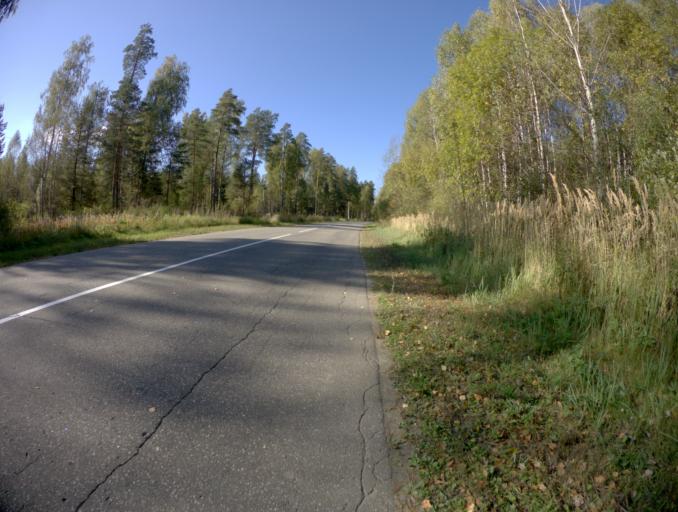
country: RU
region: Vladimir
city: Kameshkovo
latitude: 56.3484
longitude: 40.8458
